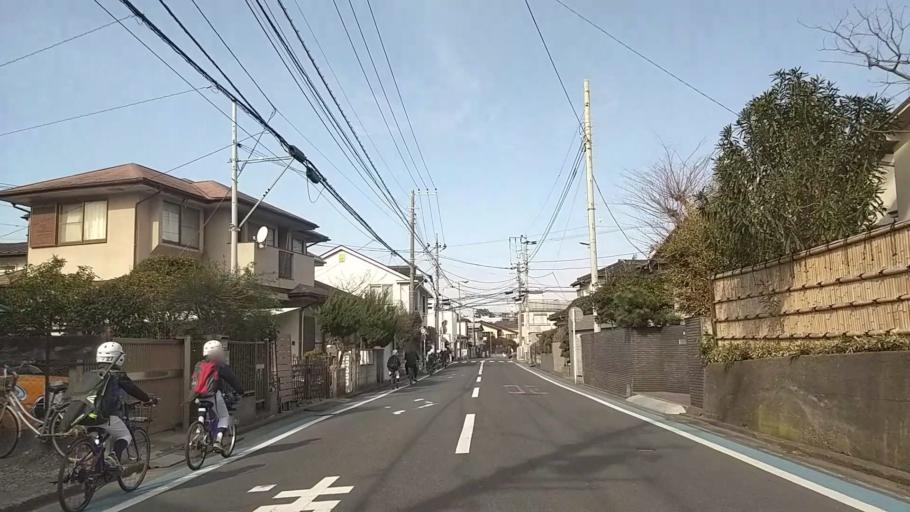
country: JP
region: Kanagawa
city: Chigasaki
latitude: 35.3204
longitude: 139.3998
